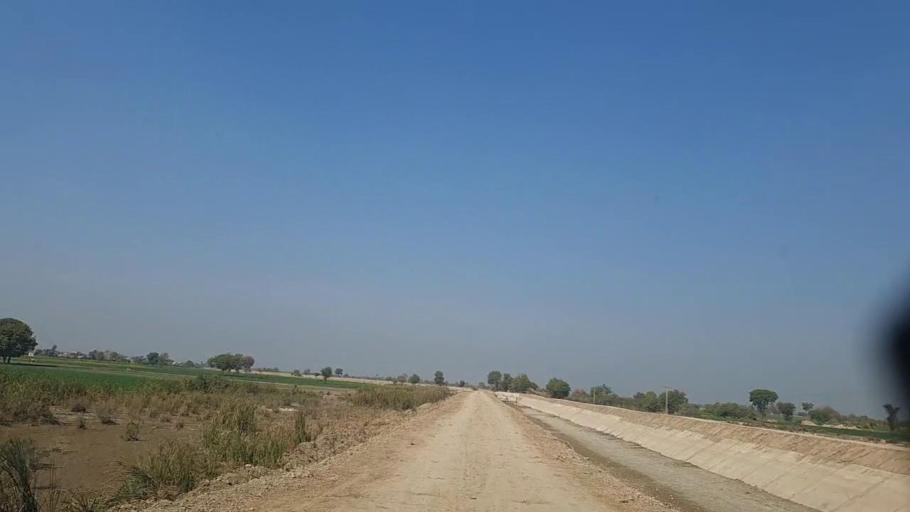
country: PK
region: Sindh
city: Sakrand
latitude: 26.1608
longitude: 68.3265
